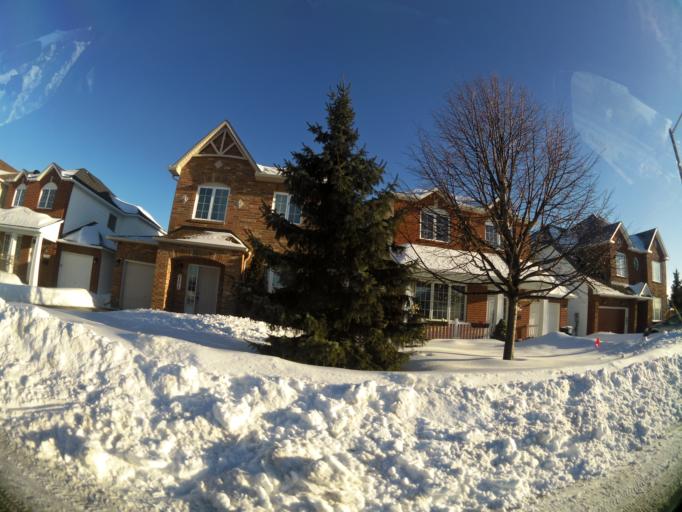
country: CA
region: Ontario
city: Ottawa
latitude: 45.4345
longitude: -75.5305
